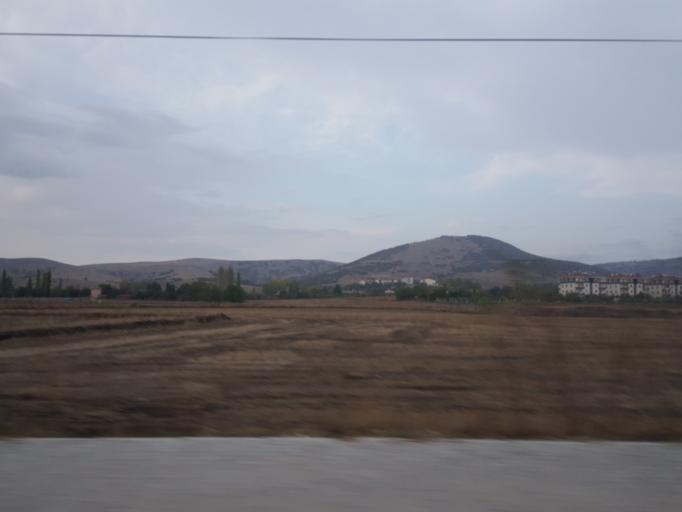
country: TR
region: Amasya
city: Gumushacikoy
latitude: 40.8847
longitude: 35.2117
